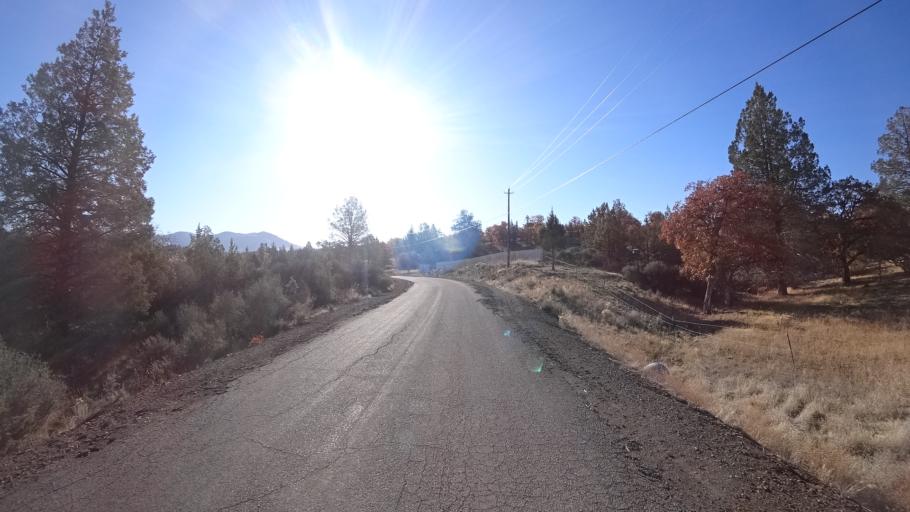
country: US
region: California
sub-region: Siskiyou County
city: Montague
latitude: 41.8815
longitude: -122.4528
